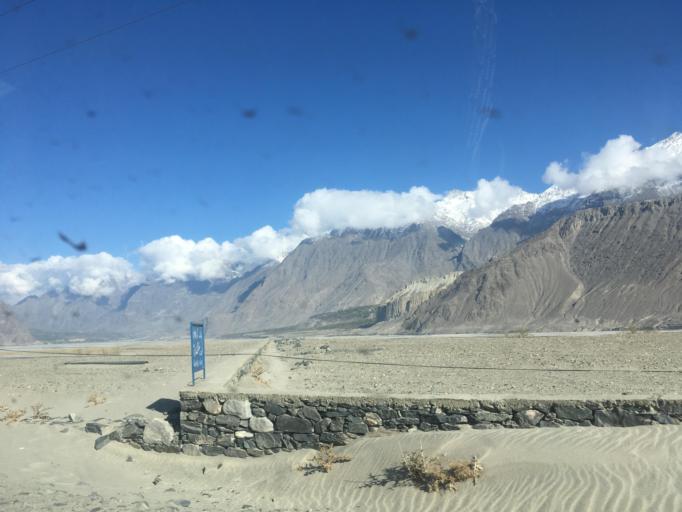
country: PK
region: Gilgit-Baltistan
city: Skardu
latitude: 35.3595
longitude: 75.5326
